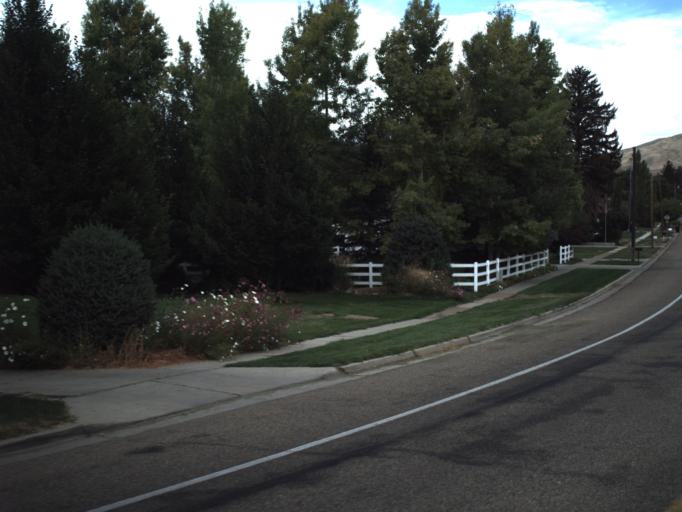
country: US
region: Utah
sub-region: Morgan County
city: Morgan
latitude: 41.0300
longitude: -111.6744
